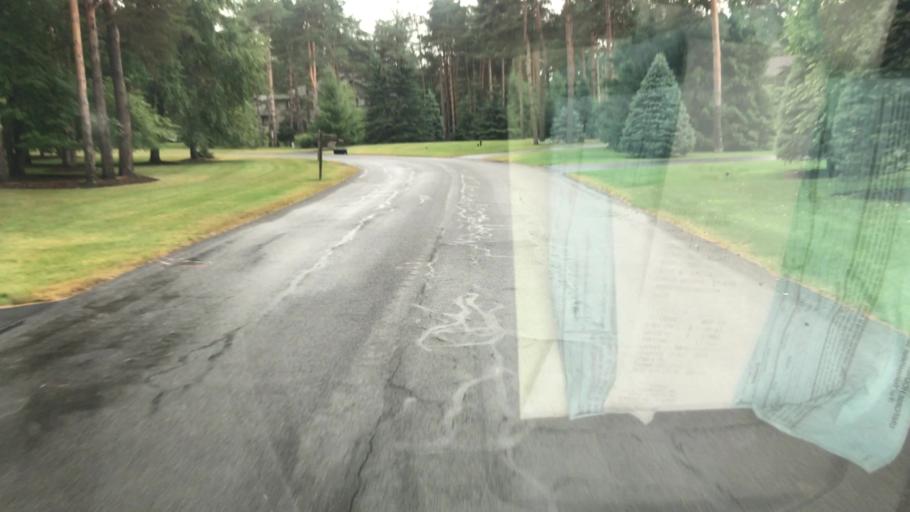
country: US
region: New York
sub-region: Onondaga County
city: Manlius
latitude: 42.9857
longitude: -75.9776
